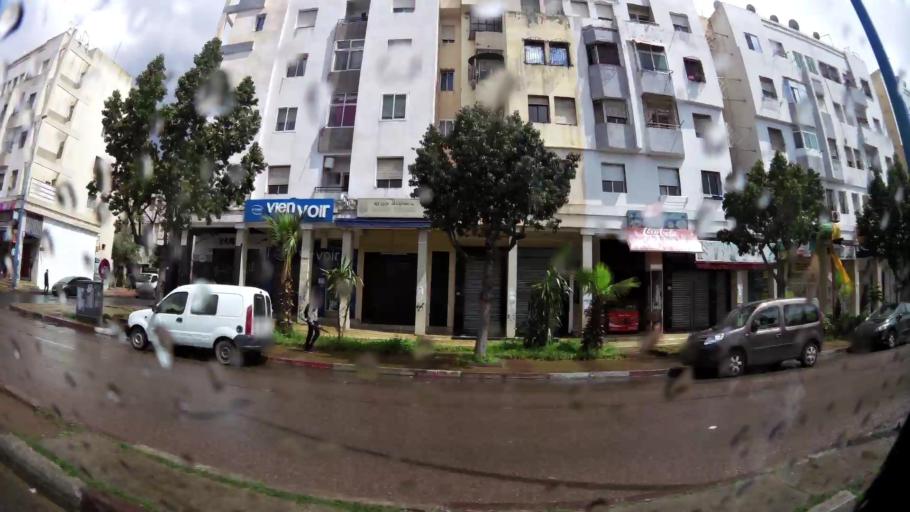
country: MA
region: Grand Casablanca
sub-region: Casablanca
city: Casablanca
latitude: 33.5295
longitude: -7.6486
